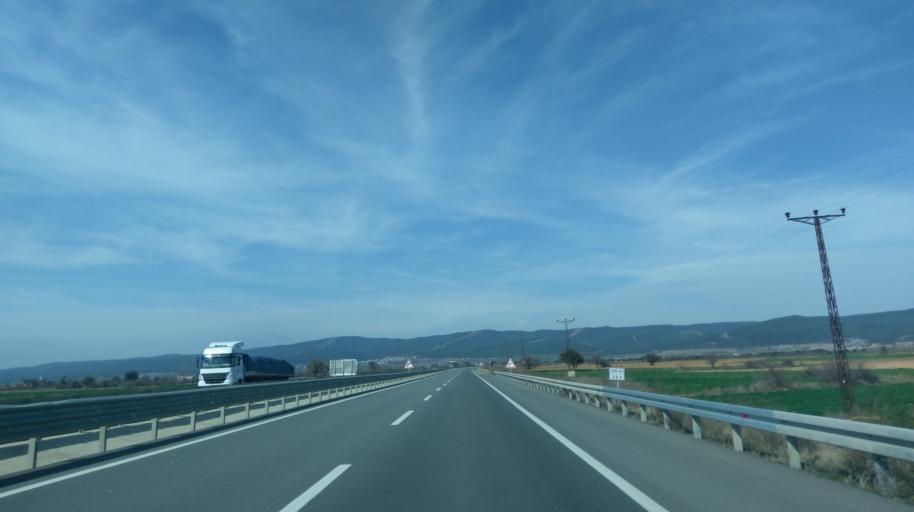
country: TR
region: Canakkale
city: Evrese
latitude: 40.6618
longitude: 26.8125
